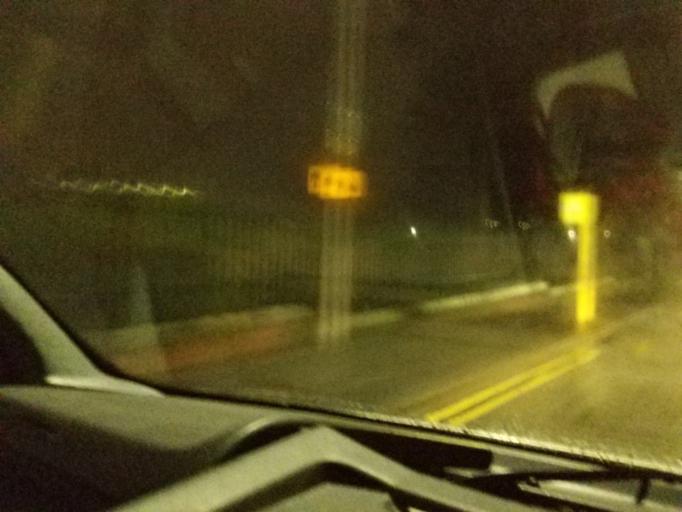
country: GB
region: England
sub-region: St. Helens
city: St Helens
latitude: 53.4616
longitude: -2.7410
